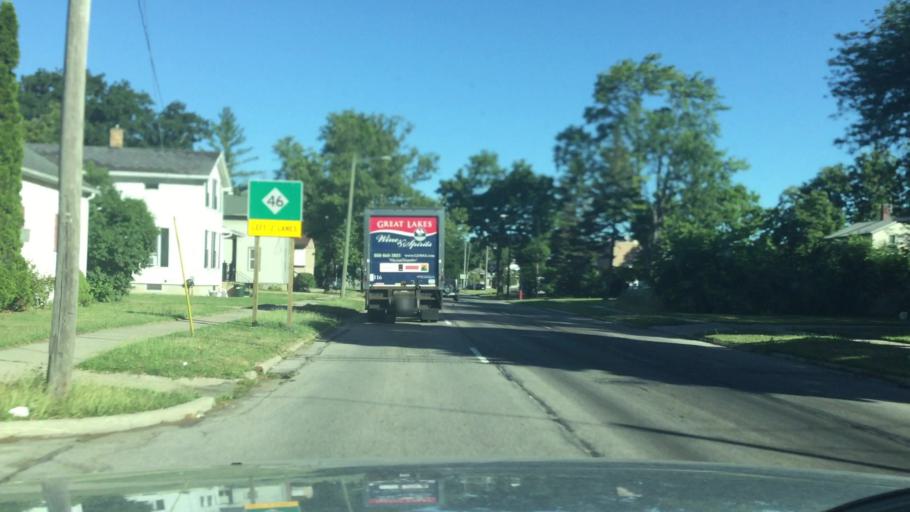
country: US
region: Michigan
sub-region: Saginaw County
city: Saginaw
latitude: 43.4137
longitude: -83.9709
